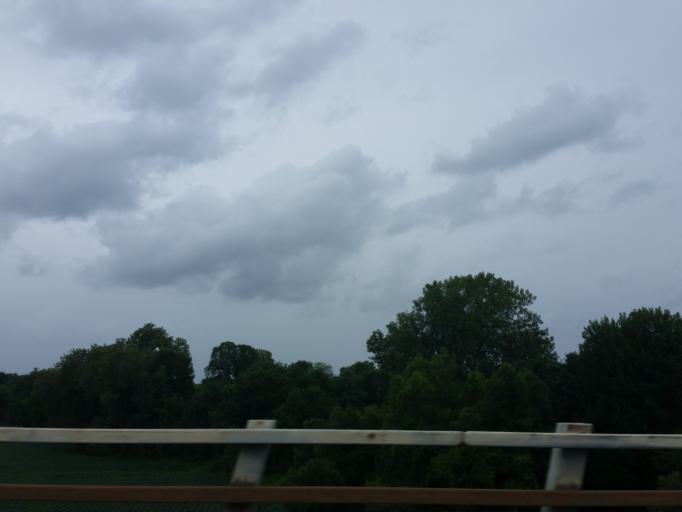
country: US
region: Illinois
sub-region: Alexander County
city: Cairo
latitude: 36.9991
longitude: -89.1403
